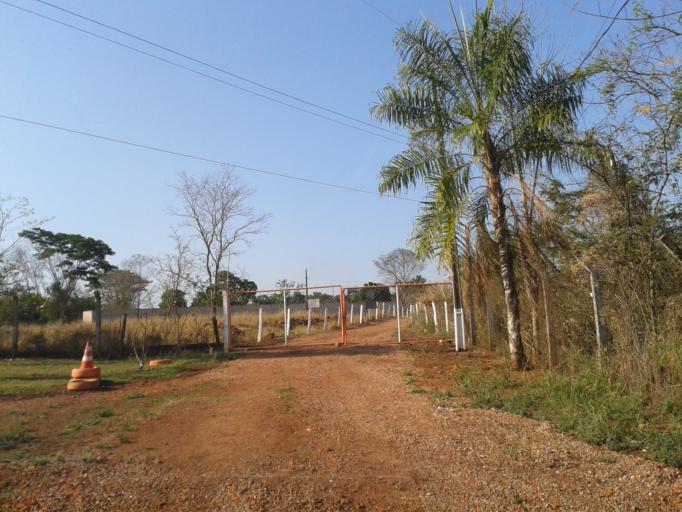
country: BR
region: Minas Gerais
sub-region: Ituiutaba
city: Ituiutaba
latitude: -18.9434
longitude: -49.4619
